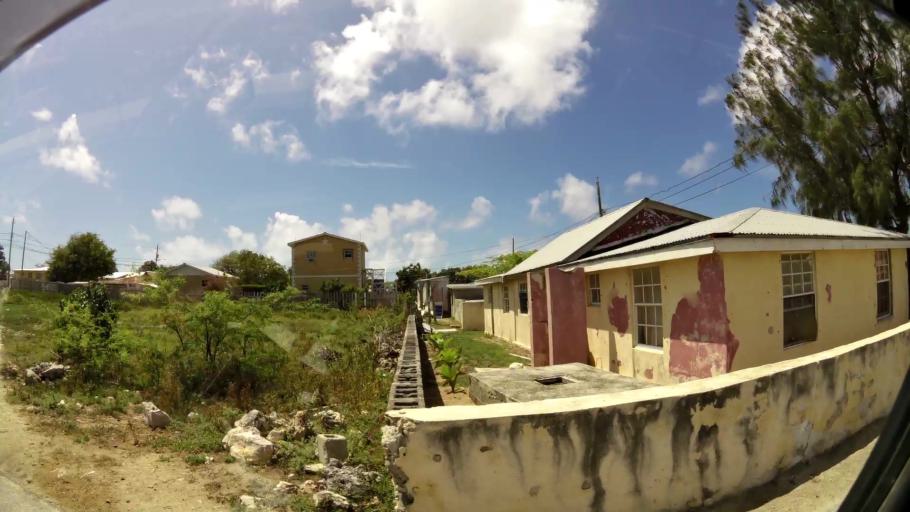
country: TC
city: Cockburn Town
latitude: 21.4776
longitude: -71.1456
